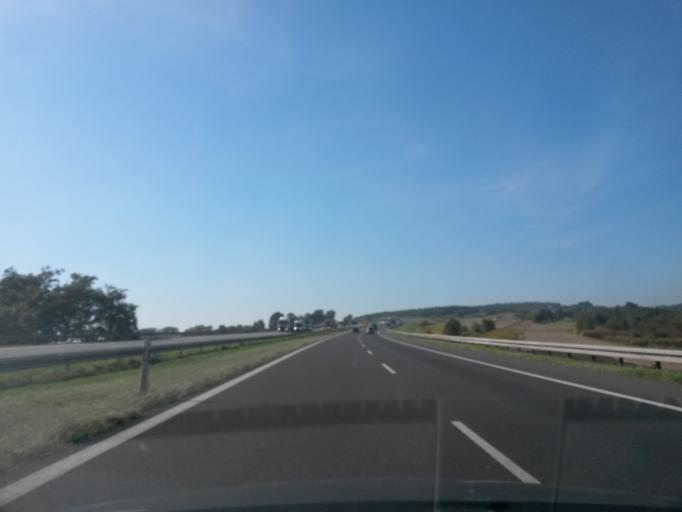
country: PL
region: Lesser Poland Voivodeship
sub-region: Powiat krakowski
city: Mnikow
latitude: 50.0760
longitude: 19.7335
